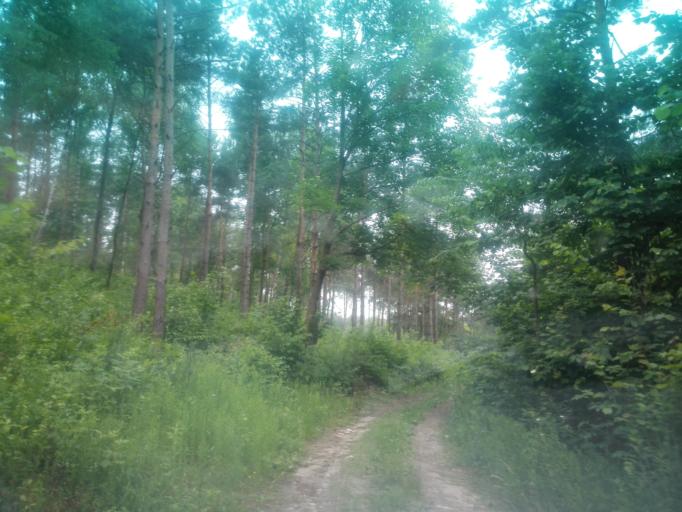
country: PL
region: Silesian Voivodeship
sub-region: Powiat czestochowski
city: Olsztyn
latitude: 50.7929
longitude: 19.2519
